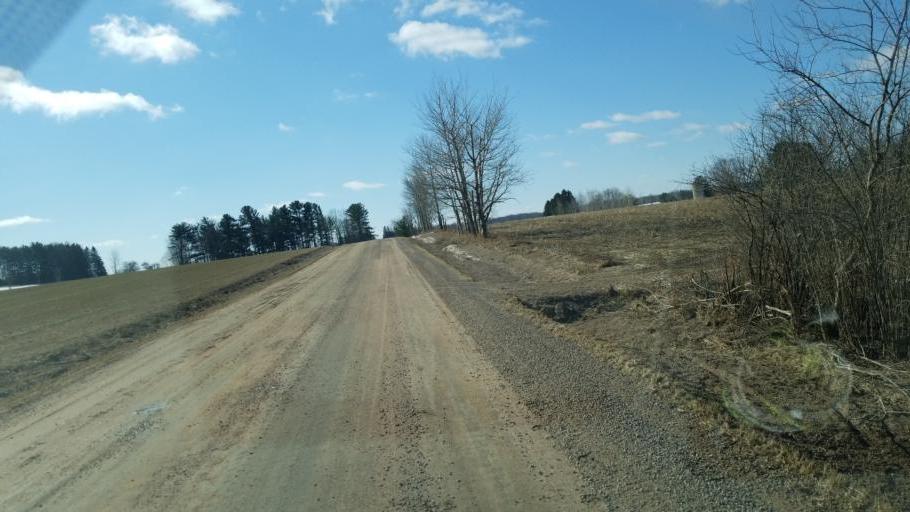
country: US
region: Wisconsin
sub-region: Clark County
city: Loyal
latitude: 44.6581
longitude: -90.4562
